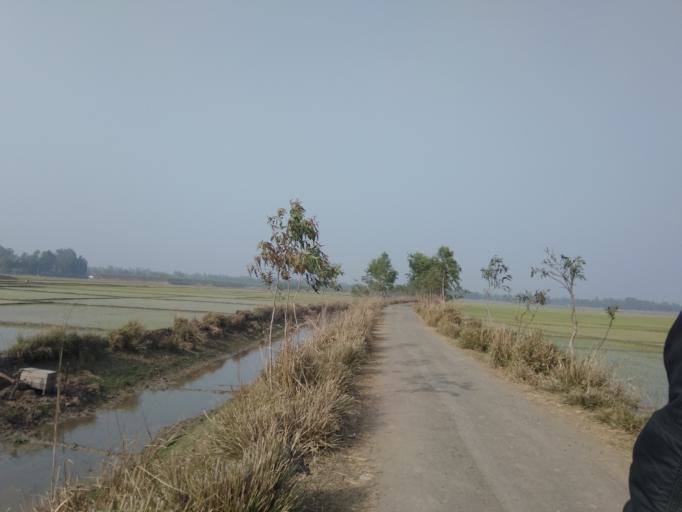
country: BD
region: Rajshahi
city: Bogra
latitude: 24.4690
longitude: 89.2678
